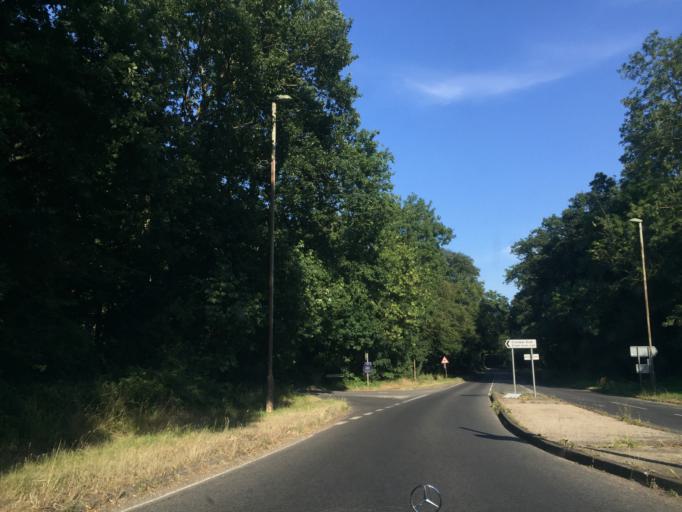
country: GB
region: England
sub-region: Oxfordshire
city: Rotherfield Peppard
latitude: 51.5744
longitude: -0.9858
